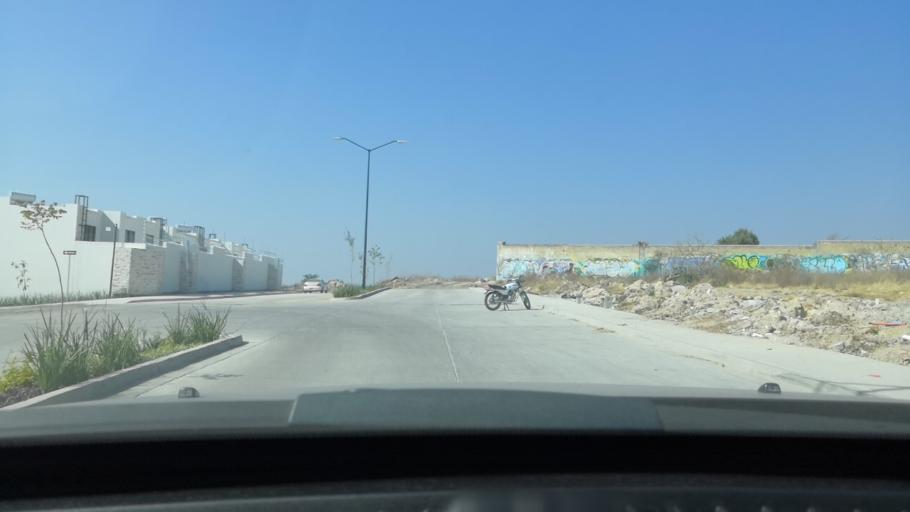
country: MX
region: Guanajuato
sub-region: Leon
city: La Ermita
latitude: 21.1633
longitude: -101.7381
